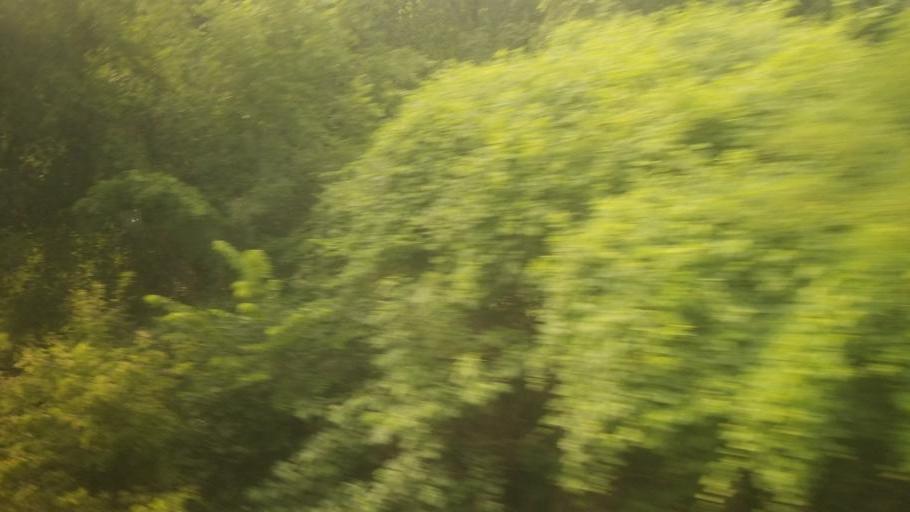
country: US
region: Kansas
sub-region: Douglas County
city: Lawrence
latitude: 39.0322
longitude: -95.3491
